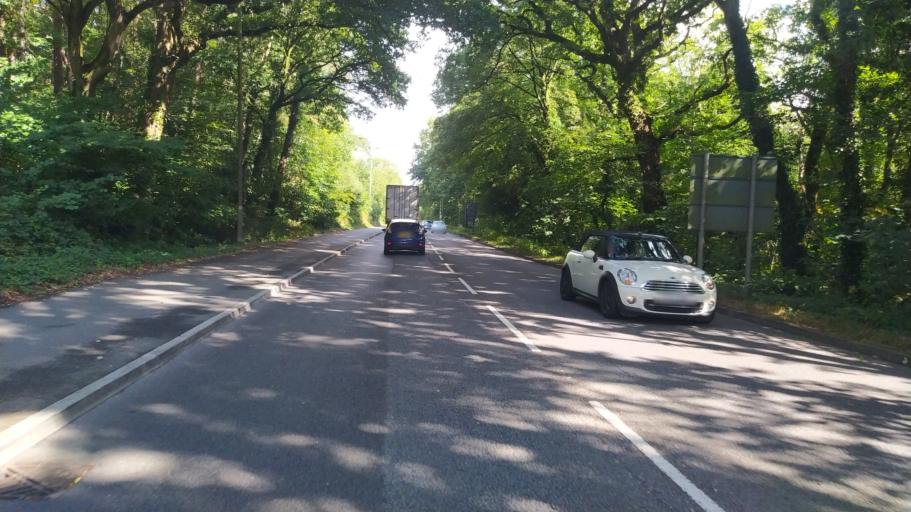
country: GB
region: England
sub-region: Dorset
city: Broadstone
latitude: 50.7652
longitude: -1.9789
